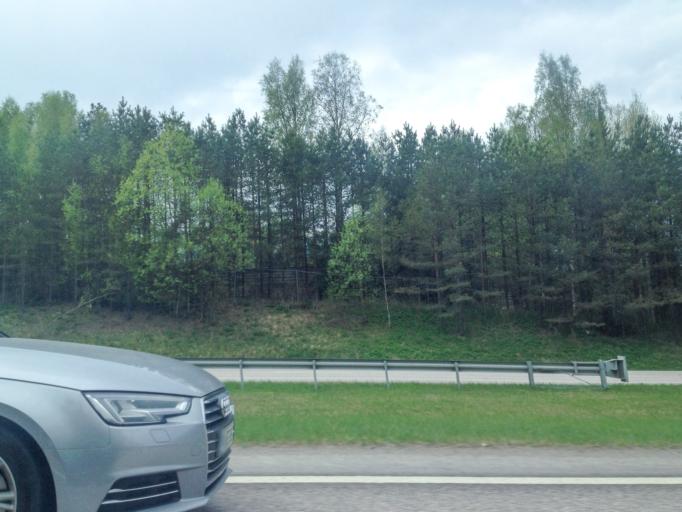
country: FI
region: Uusimaa
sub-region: Helsinki
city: Hyvinge
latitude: 60.5907
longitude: 24.7978
